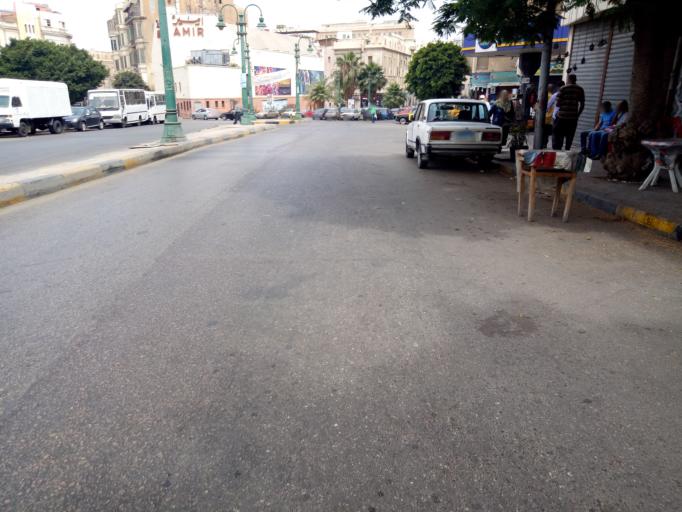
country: EG
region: Alexandria
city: Alexandria
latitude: 31.1962
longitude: 29.9050
